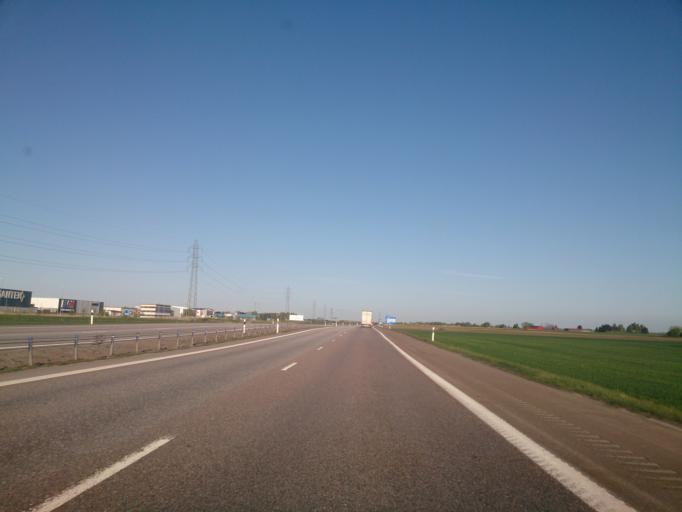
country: SE
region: OEstergoetland
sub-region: Linkopings Kommun
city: Linkoping
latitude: 58.4354
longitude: 15.6062
